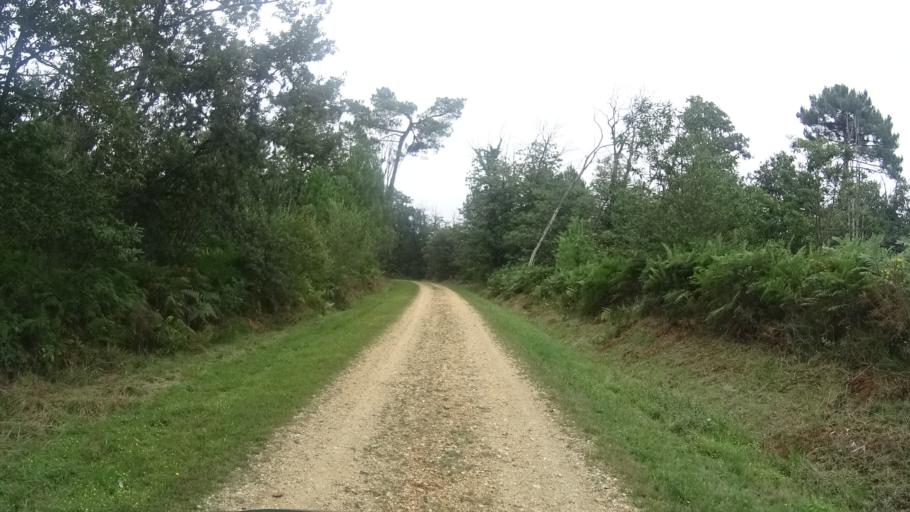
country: FR
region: Aquitaine
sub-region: Departement de la Dordogne
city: Sourzac
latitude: 45.0333
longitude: 0.4105
